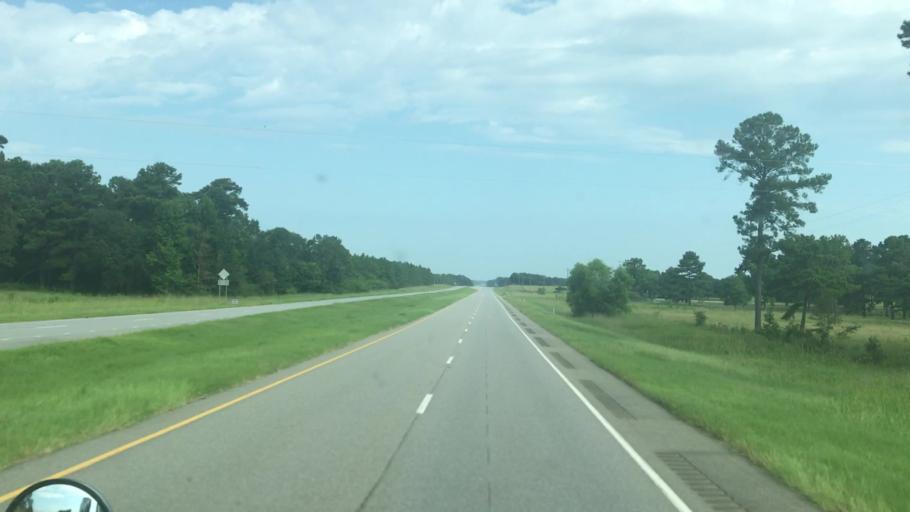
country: US
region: Georgia
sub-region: Early County
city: Blakely
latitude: 31.3225
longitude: -84.8845
